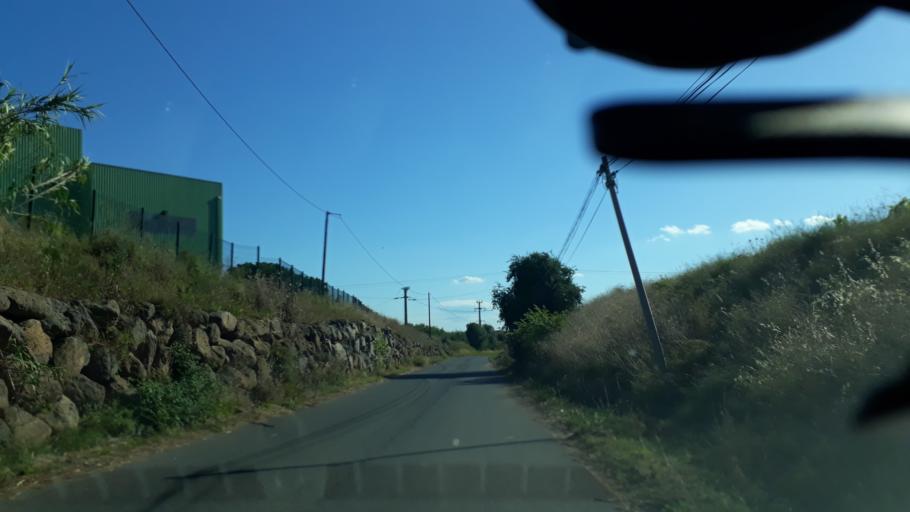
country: FR
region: Languedoc-Roussillon
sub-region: Departement de l'Herault
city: Agde
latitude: 43.3222
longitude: 3.4914
